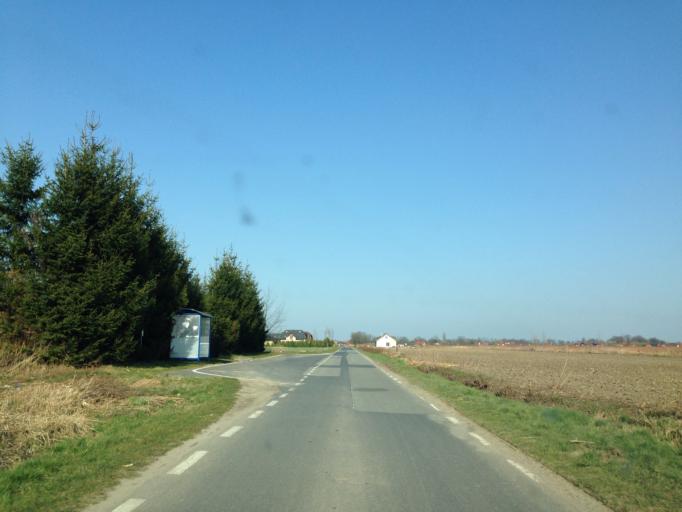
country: PL
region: Lower Silesian Voivodeship
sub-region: Powiat wroclawski
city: Kamieniec Wroclawski
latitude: 51.0966
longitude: 17.2043
